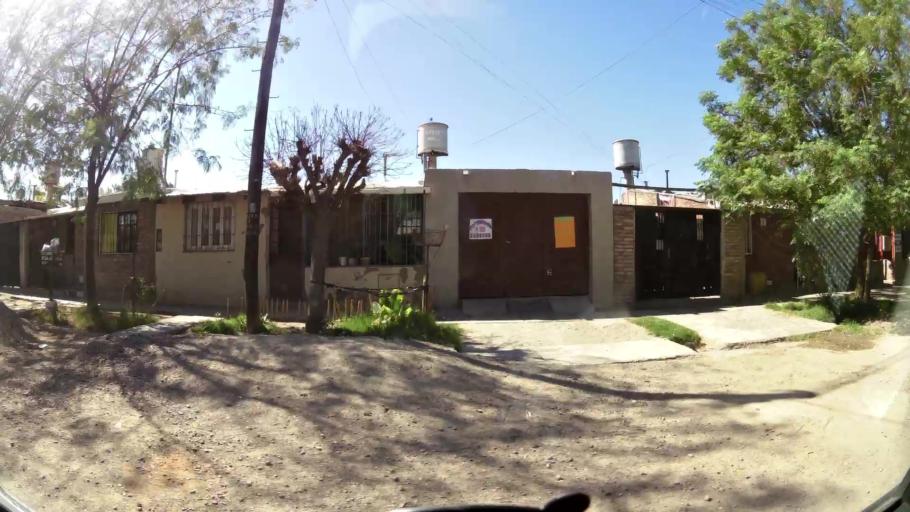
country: AR
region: Mendoza
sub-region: Departamento de Godoy Cruz
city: Godoy Cruz
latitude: -32.9639
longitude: -68.8358
